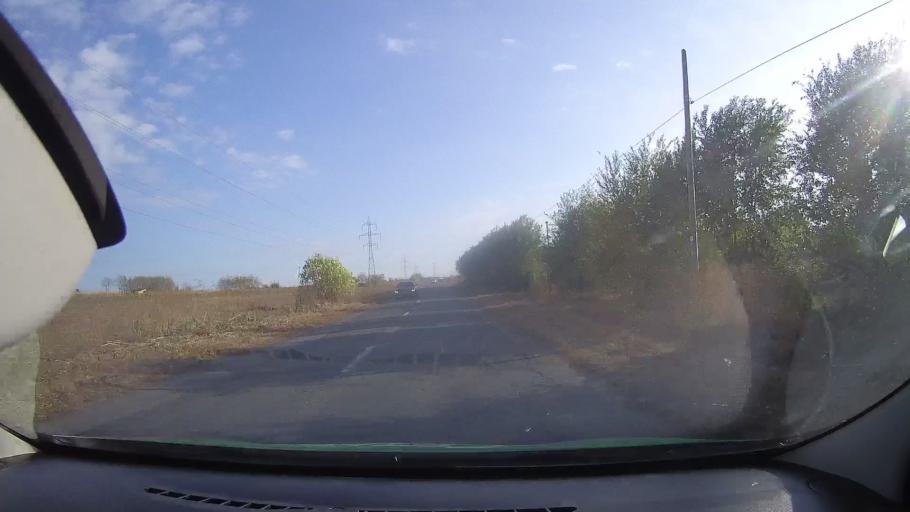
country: RO
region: Constanta
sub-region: Comuna Corbu
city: Corbu
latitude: 44.3709
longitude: 28.6673
